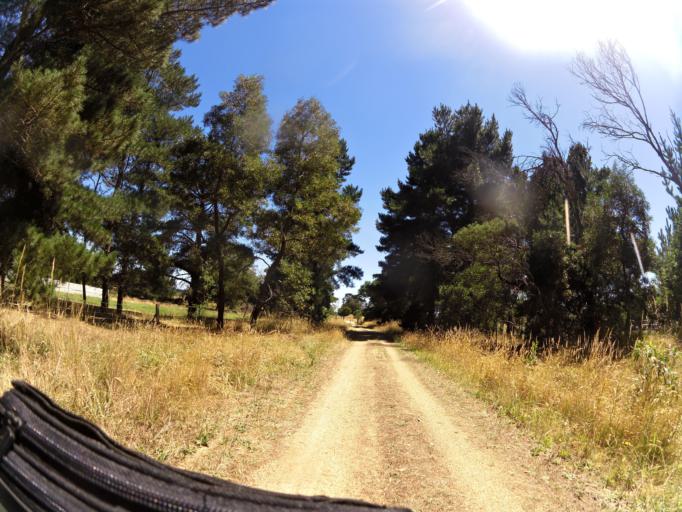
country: AU
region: Victoria
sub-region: Ballarat North
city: Delacombe
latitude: -37.6987
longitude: 143.6548
